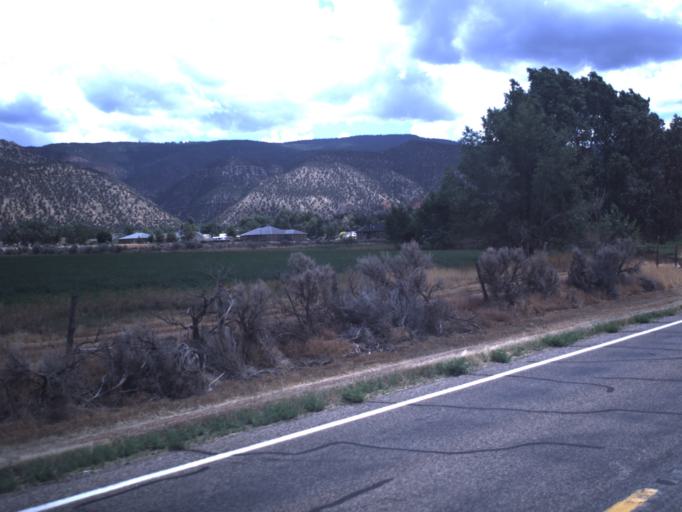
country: US
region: Utah
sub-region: Iron County
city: Parowan
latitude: 37.8935
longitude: -112.7749
